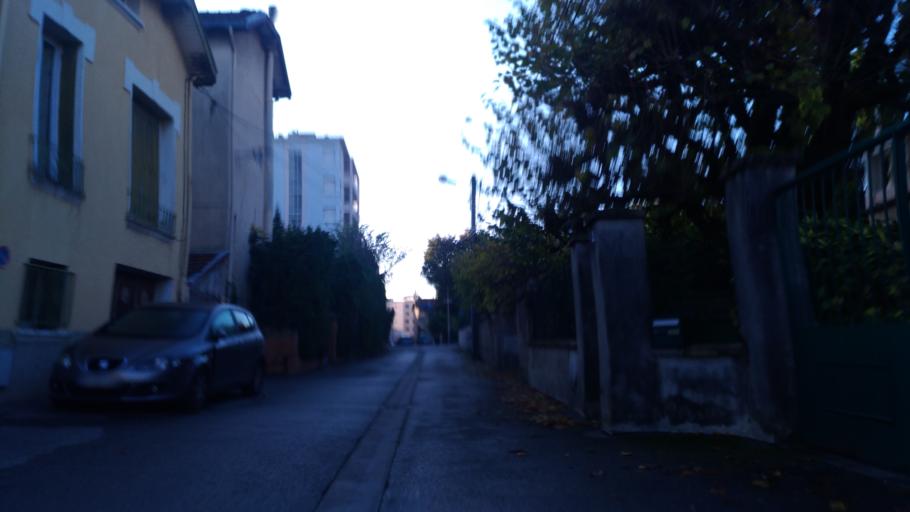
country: FR
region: Rhone-Alpes
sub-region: Departement de l'Isere
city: Fontaine
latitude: 45.1928
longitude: 5.6894
